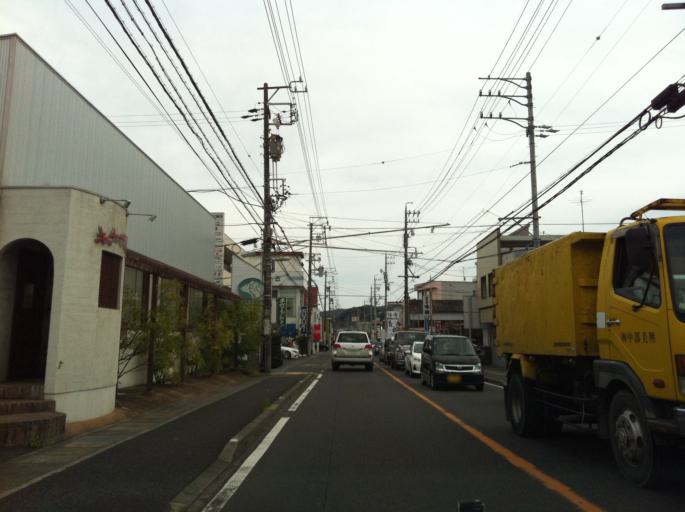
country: JP
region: Shizuoka
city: Shizuoka-shi
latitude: 35.0090
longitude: 138.4639
